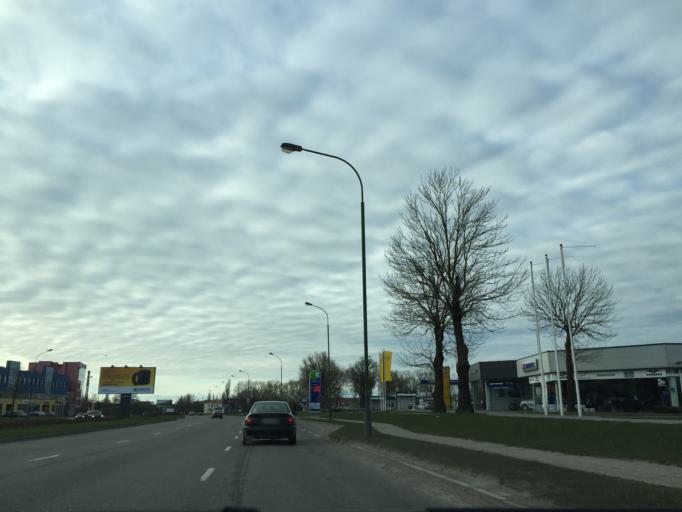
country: LT
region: Klaipedos apskritis
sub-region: Klaipeda
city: Klaipeda
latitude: 55.7022
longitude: 21.1654
